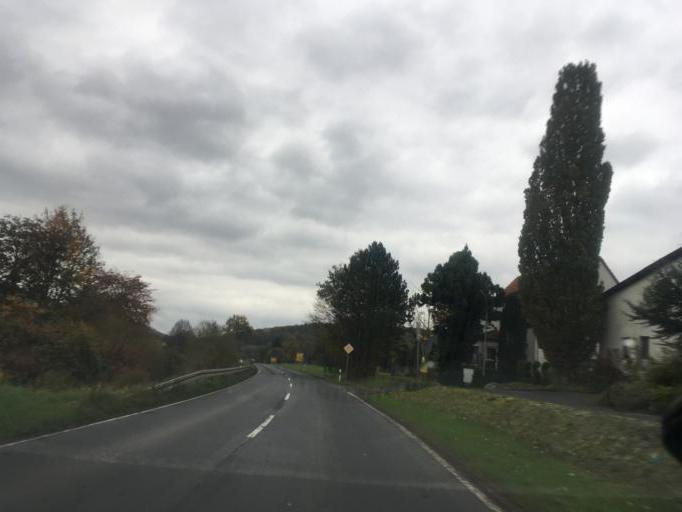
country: DE
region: Lower Saxony
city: Bodenfelde
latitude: 51.6227
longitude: 9.5630
